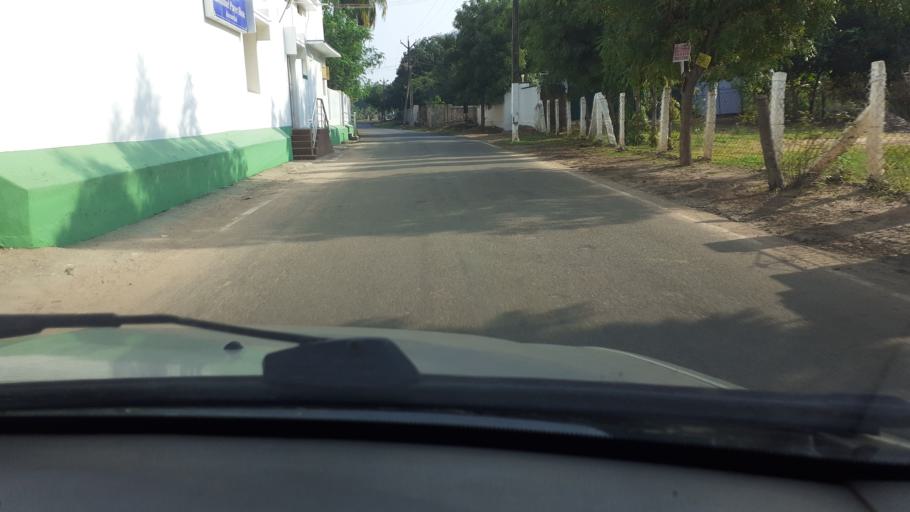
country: IN
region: Tamil Nadu
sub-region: Thoothukkudi
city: Eral
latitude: 8.5776
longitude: 78.0221
